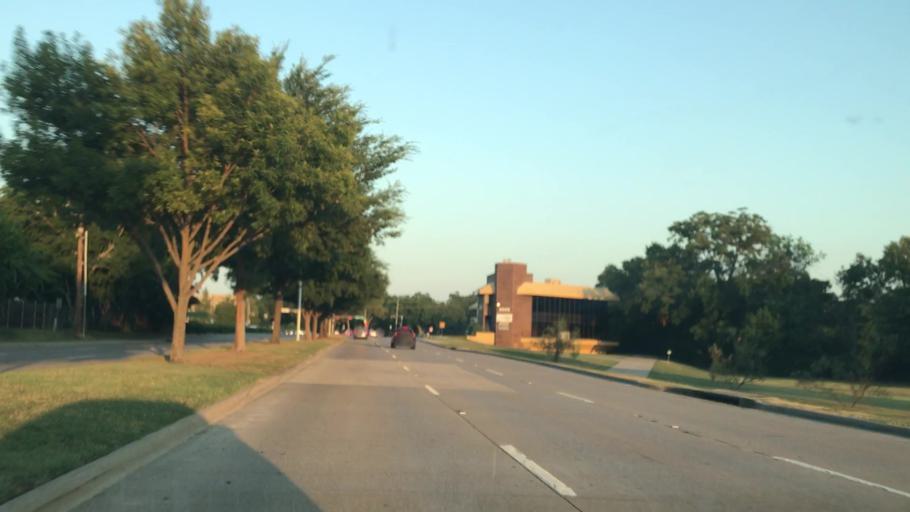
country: US
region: Texas
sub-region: Dallas County
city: Richardson
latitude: 32.8947
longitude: -96.7556
